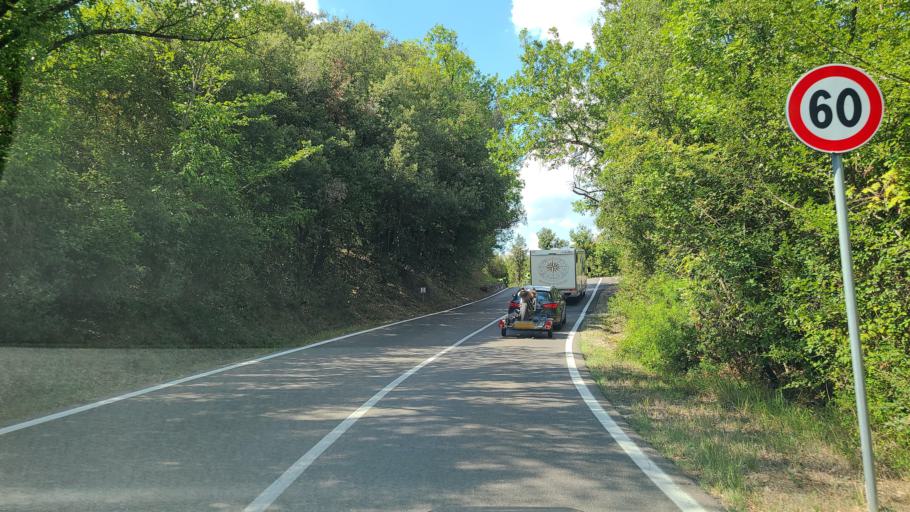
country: IT
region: Tuscany
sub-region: Provincia di Siena
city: San Gimignano
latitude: 43.4020
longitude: 10.9962
